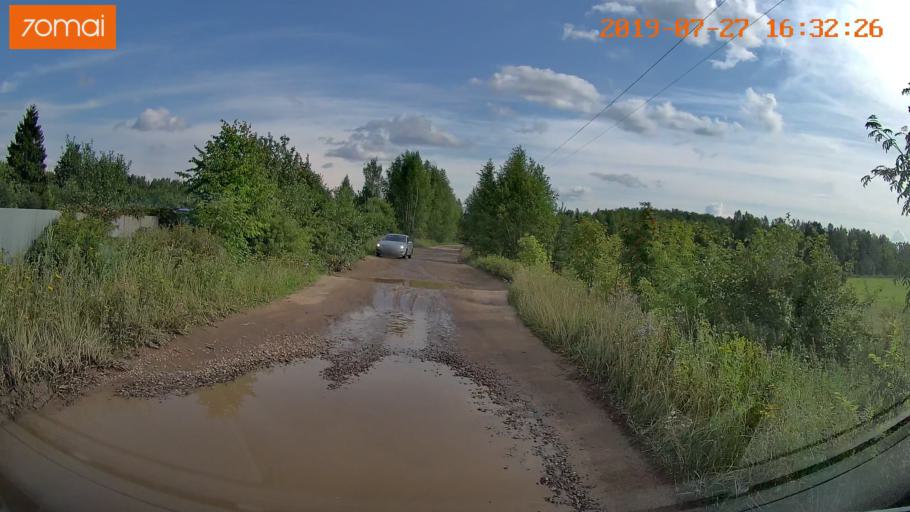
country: RU
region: Ivanovo
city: Novo-Talitsy
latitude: 57.0897
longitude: 40.8515
